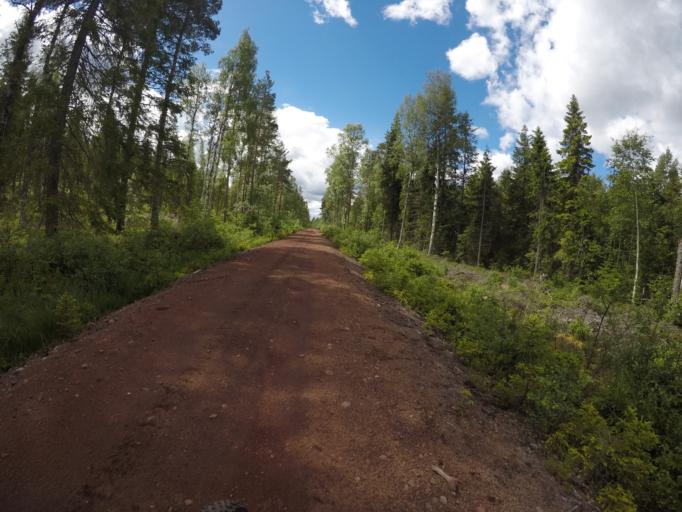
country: SE
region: Vaermland
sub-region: Filipstads Kommun
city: Lesjofors
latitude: 60.1389
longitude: 14.3425
